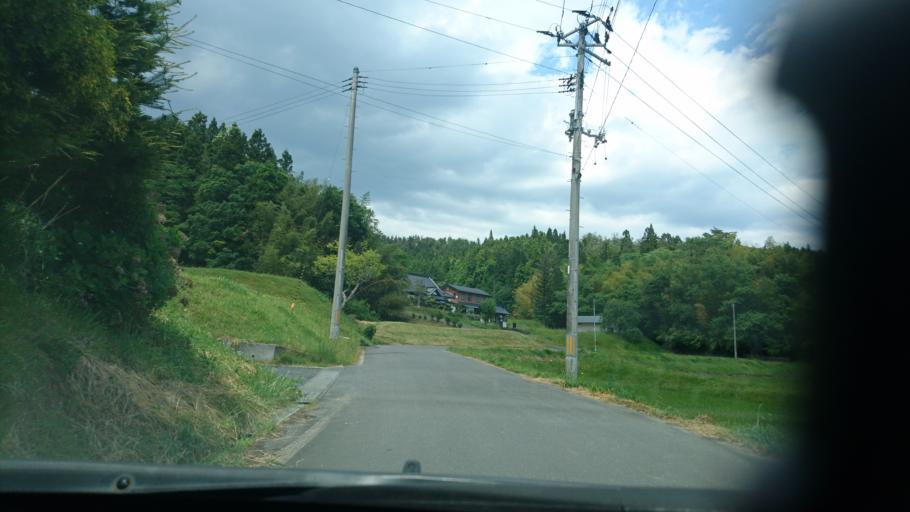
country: JP
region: Iwate
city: Ichinoseki
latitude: 38.9779
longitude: 141.0909
